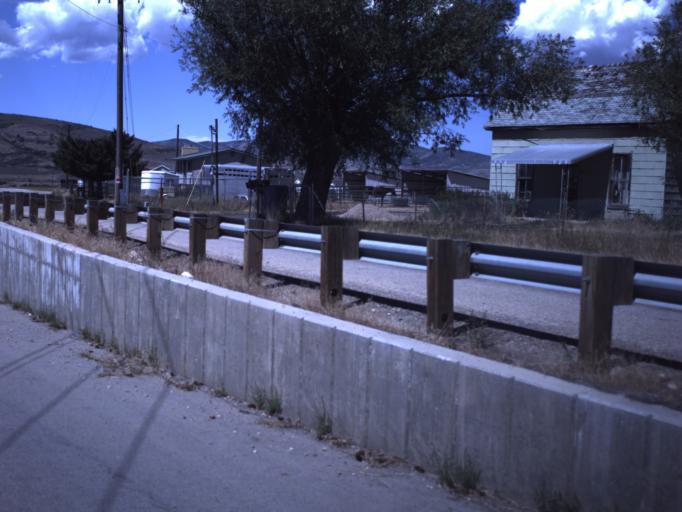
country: US
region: Utah
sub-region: Summit County
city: Francis
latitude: 40.6105
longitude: -111.2859
